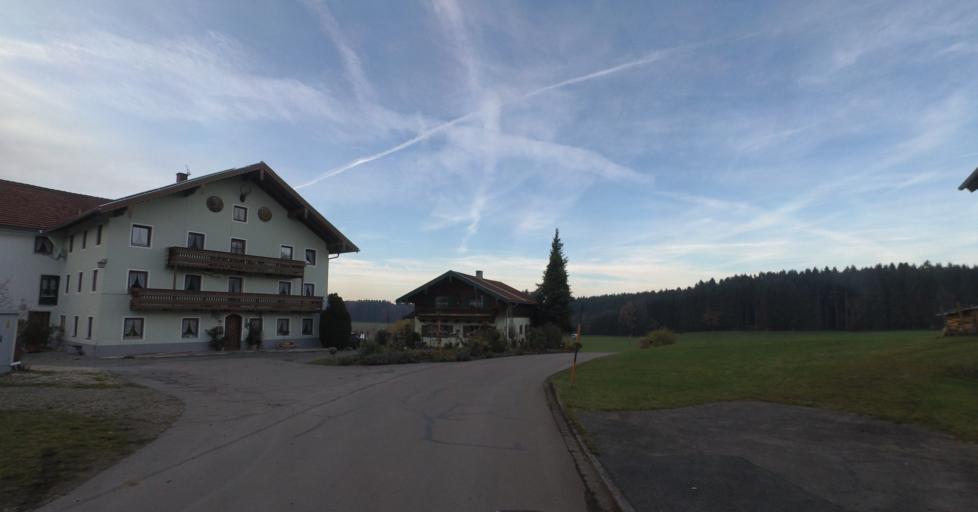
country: DE
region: Bavaria
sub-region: Upper Bavaria
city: Nussdorf
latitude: 47.8935
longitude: 12.5967
